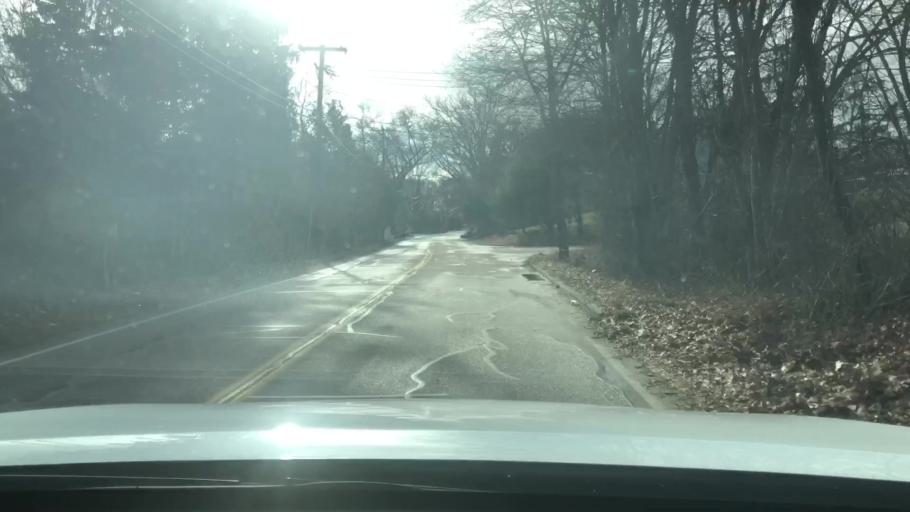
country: US
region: Massachusetts
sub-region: Worcester County
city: Blackstone
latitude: 42.0217
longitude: -71.5252
